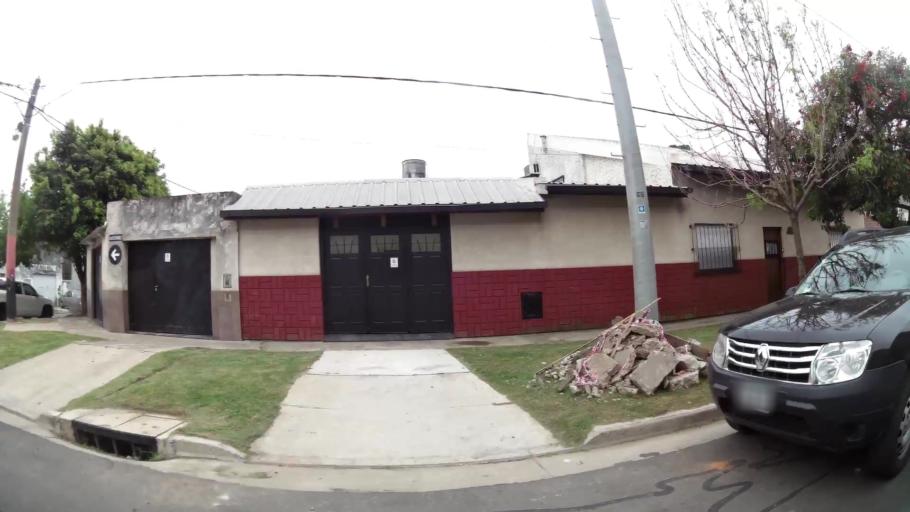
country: AR
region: Santa Fe
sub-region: Departamento de Rosario
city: Rosario
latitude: -32.9859
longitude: -60.6552
